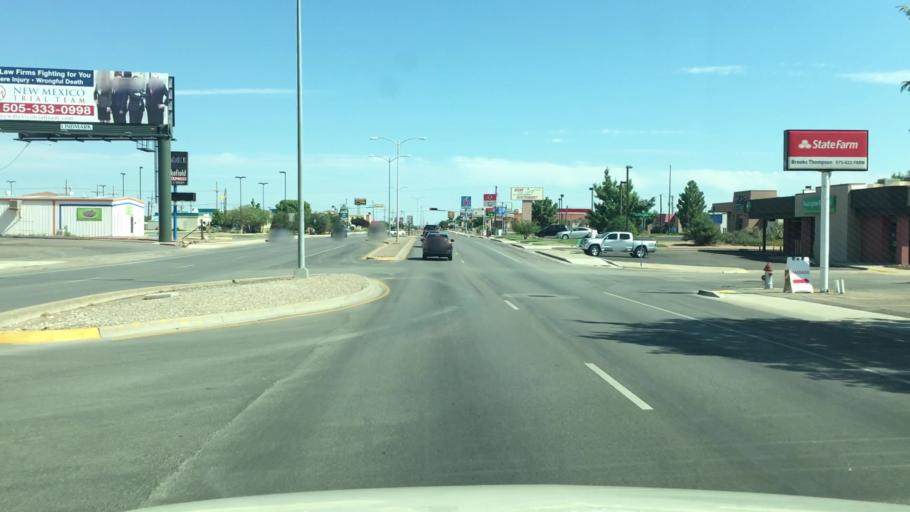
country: US
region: New Mexico
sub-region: Chaves County
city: Roswell
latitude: 33.4359
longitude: -104.5231
